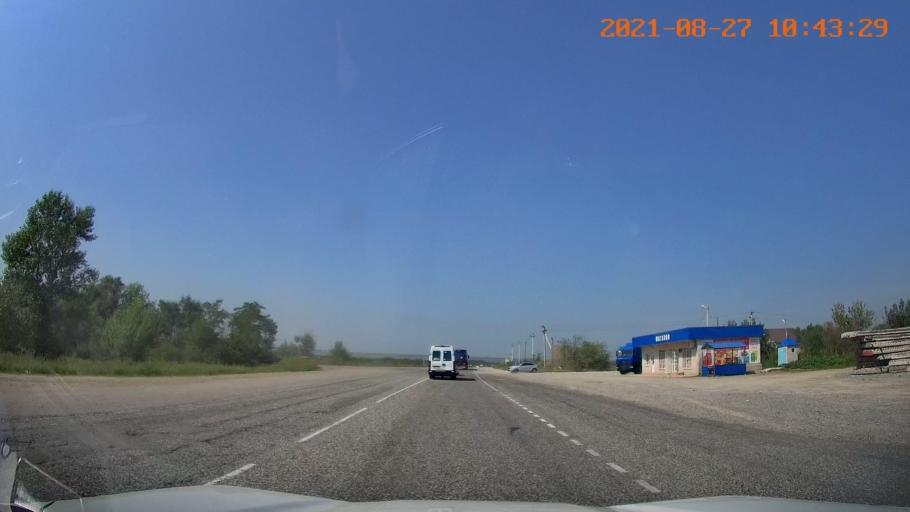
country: RU
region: Karachayevo-Cherkesiya
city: Psyzh
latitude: 44.3007
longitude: 42.0297
